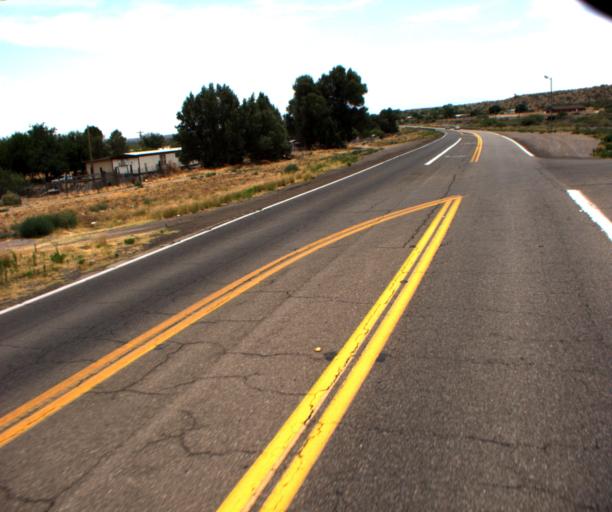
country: US
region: Arizona
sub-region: Graham County
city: Bylas
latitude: 33.1419
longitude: -110.1256
